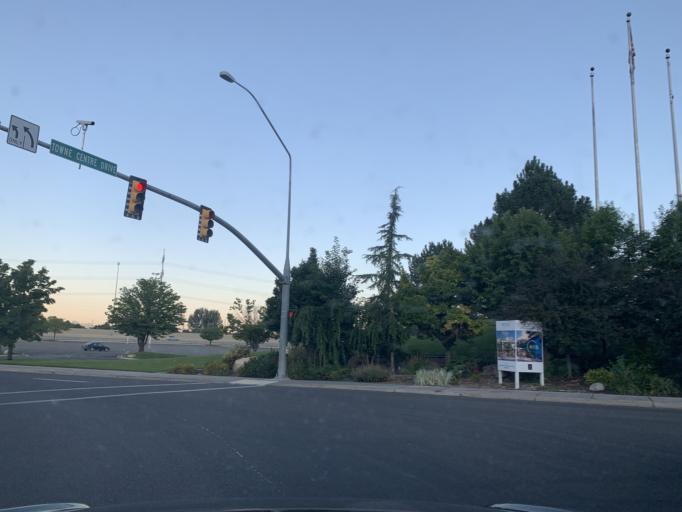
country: US
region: Utah
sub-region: Utah County
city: Provo
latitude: 40.2147
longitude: -111.6612
